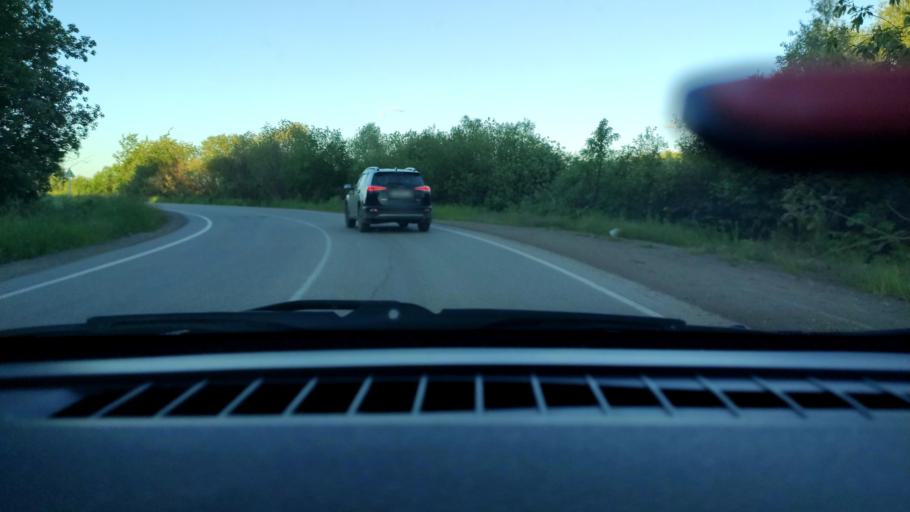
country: RU
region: Perm
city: Kultayevo
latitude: 57.9183
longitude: 55.9311
